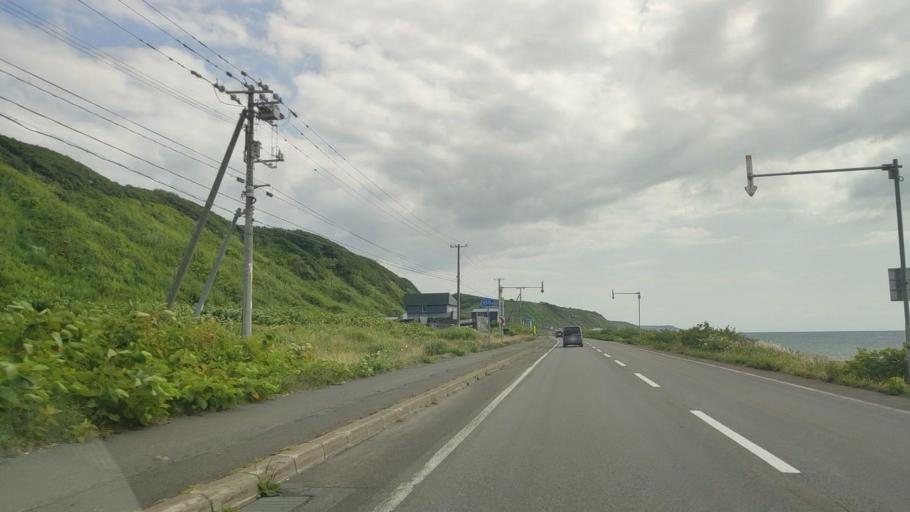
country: JP
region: Hokkaido
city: Rumoi
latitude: 44.2078
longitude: 141.6571
